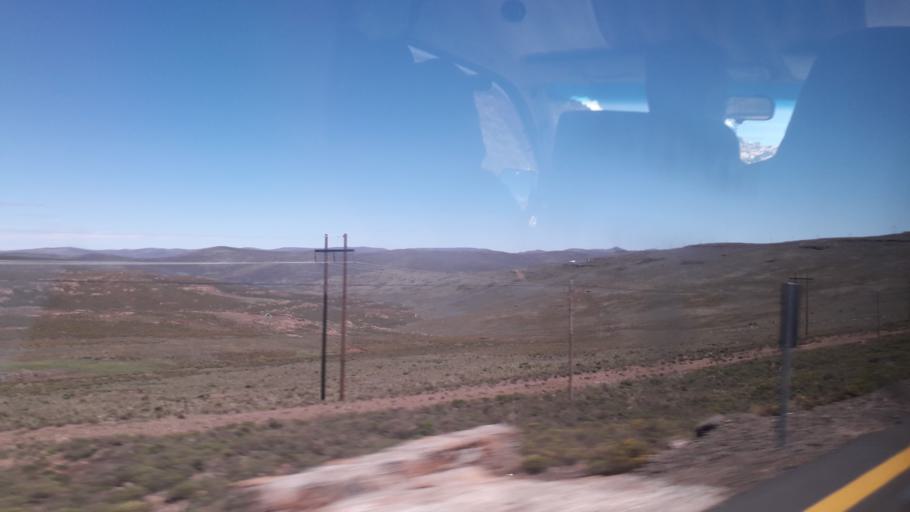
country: LS
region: Mokhotlong
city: Mokhotlong
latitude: -29.0320
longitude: 28.8609
